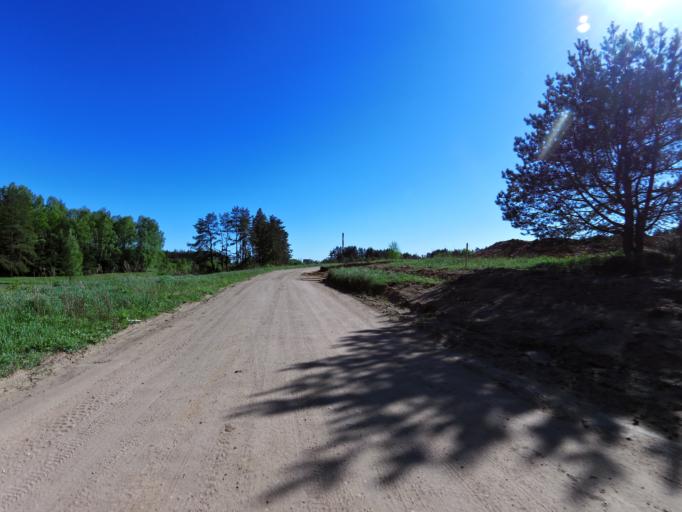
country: LT
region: Vilnius County
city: Pilaite
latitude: 54.6869
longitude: 25.1628
